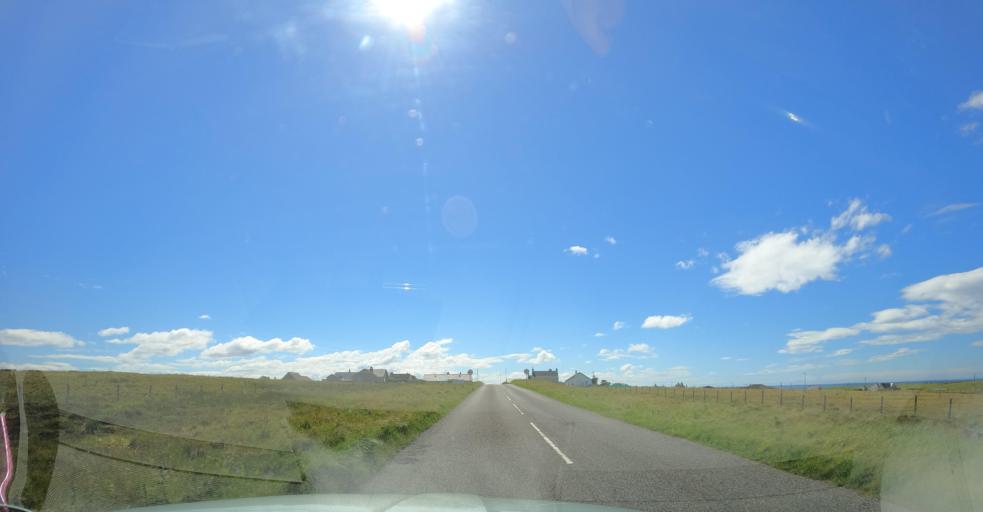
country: GB
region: Scotland
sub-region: Eilean Siar
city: Isle of Lewis
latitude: 58.4052
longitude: -6.4581
